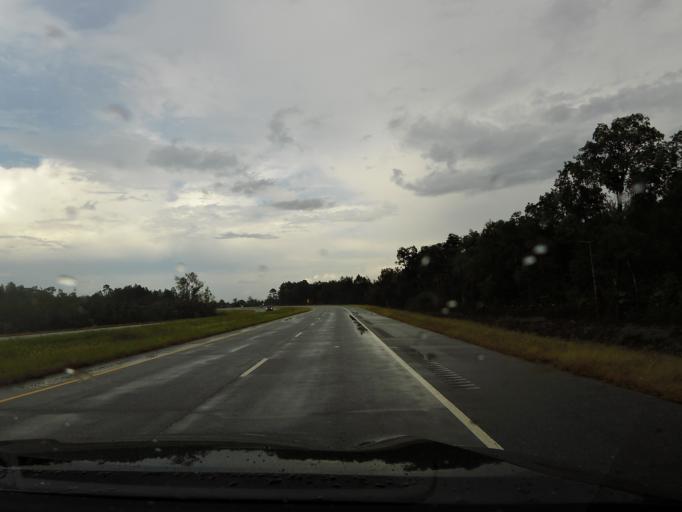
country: US
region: Georgia
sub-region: Wayne County
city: Jesup
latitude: 31.6046
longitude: -81.8617
